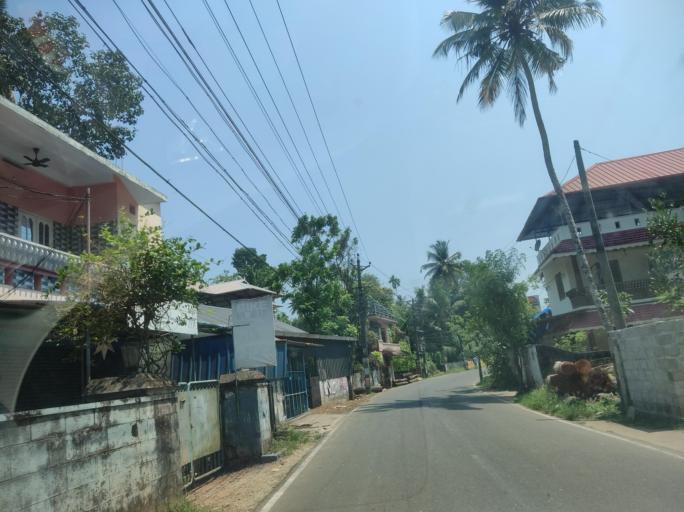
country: IN
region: Kerala
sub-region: Alappuzha
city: Kutiatodu
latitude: 9.8284
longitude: 76.2981
